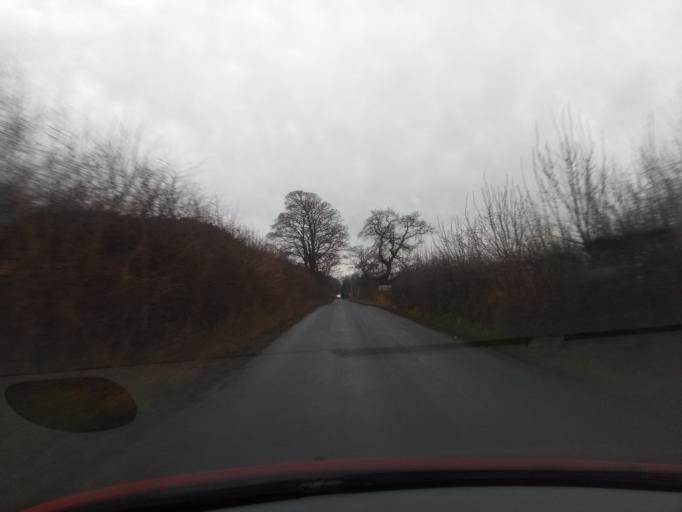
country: GB
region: England
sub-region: Northumberland
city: Whittingham
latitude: 55.4798
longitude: -1.8790
